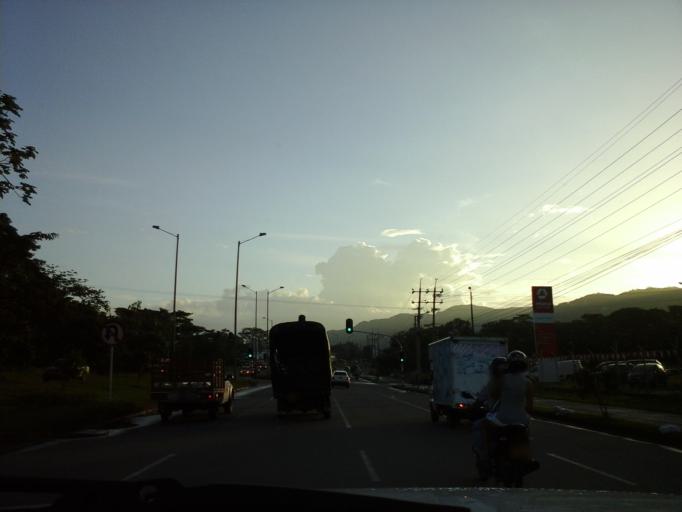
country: CO
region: Meta
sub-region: Villavicencio
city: Villavicencio
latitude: 4.1157
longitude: -73.6294
